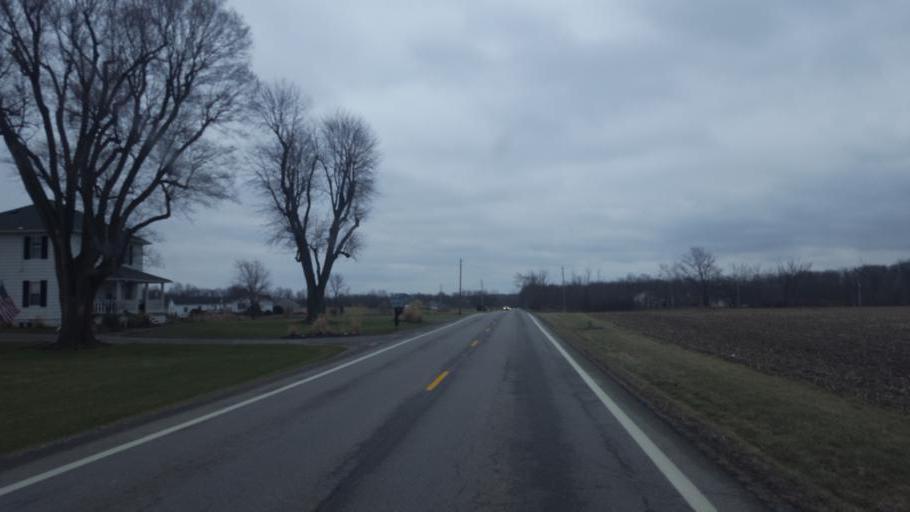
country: US
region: Ohio
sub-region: Delaware County
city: Ashley
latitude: 40.4211
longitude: -83.0298
